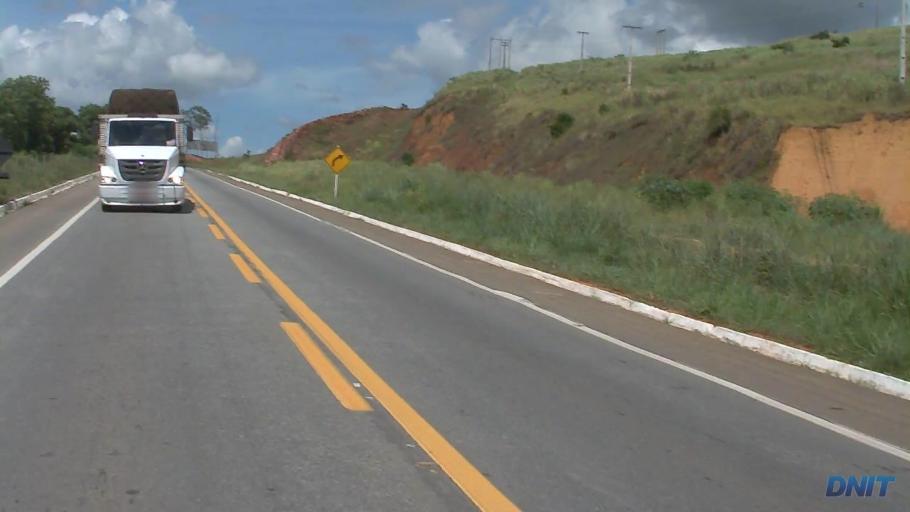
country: BR
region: Minas Gerais
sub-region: Governador Valadares
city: Governador Valadares
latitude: -18.9270
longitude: -42.0393
